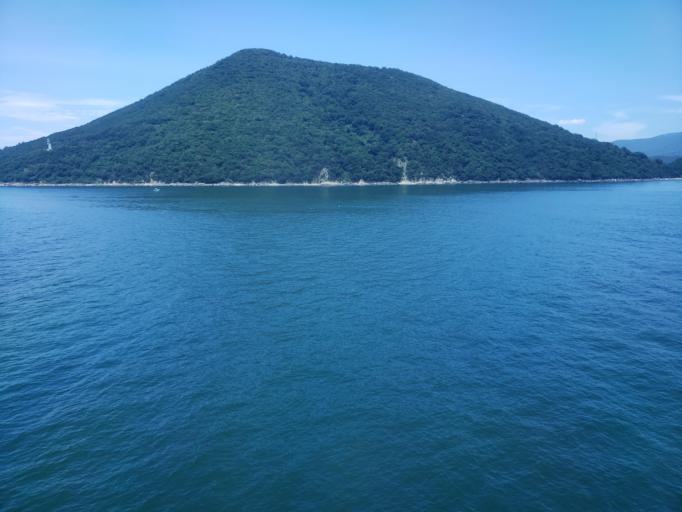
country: JP
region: Kagawa
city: Tonosho
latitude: 34.4091
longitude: 134.2440
